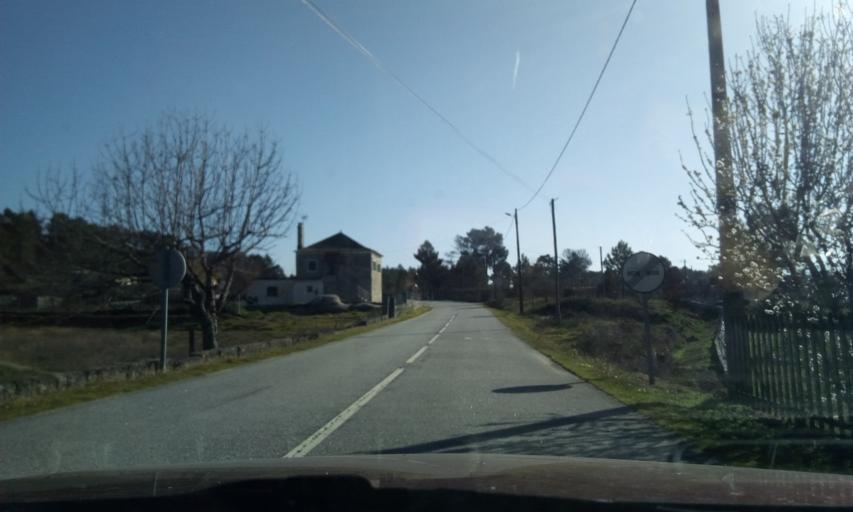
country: PT
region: Guarda
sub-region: Fornos de Algodres
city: Fornos de Algodres
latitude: 40.6334
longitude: -7.4915
